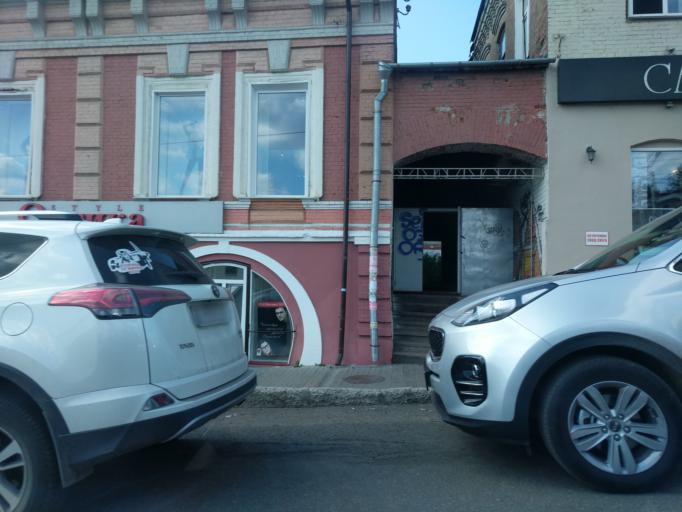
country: RU
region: Kirov
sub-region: Kirovo-Chepetskiy Rayon
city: Kirov
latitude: 58.6028
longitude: 49.6809
